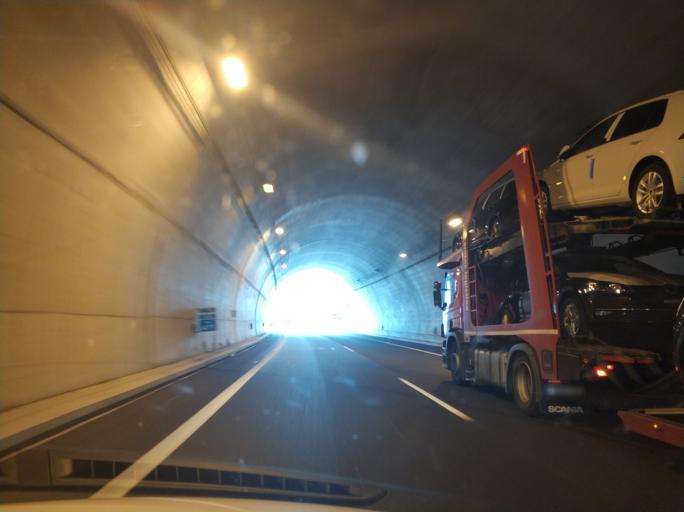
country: ES
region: Asturias
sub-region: Province of Asturias
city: Navia
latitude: 43.5419
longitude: -6.6208
